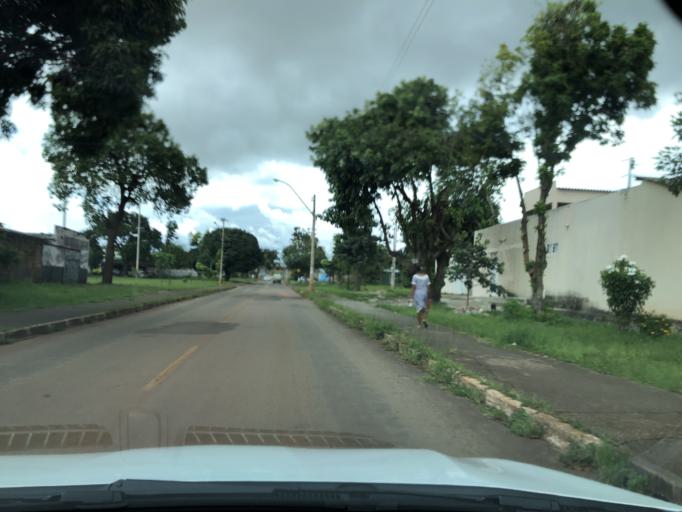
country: BR
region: Goias
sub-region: Luziania
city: Luziania
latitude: -16.0275
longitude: -48.0639
